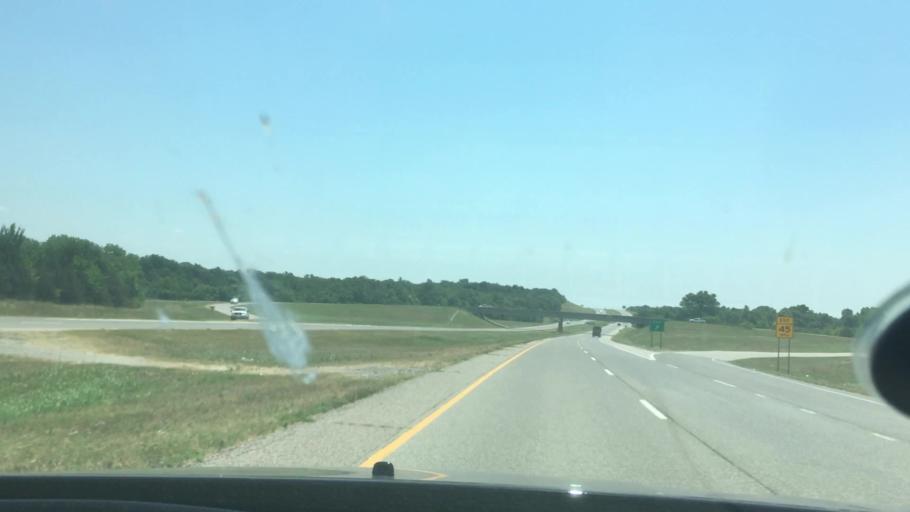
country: US
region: Oklahoma
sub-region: Pontotoc County
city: Ada
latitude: 34.7408
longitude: -96.6470
